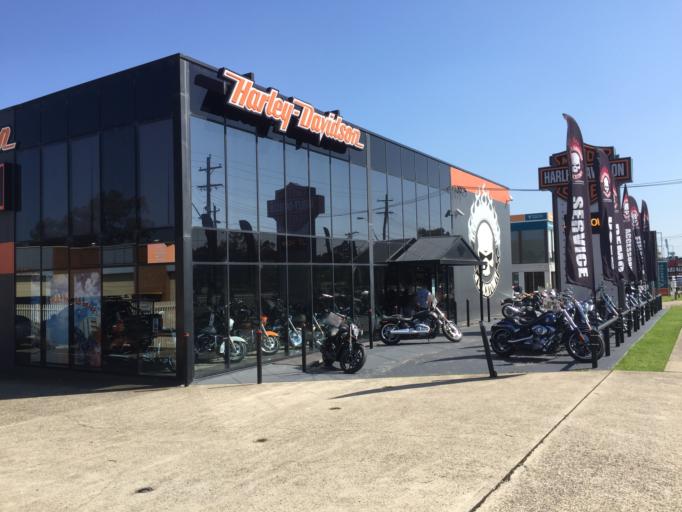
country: AU
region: New South Wales
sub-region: Blacktown
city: Blacktown
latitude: -33.7607
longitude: 150.9137
